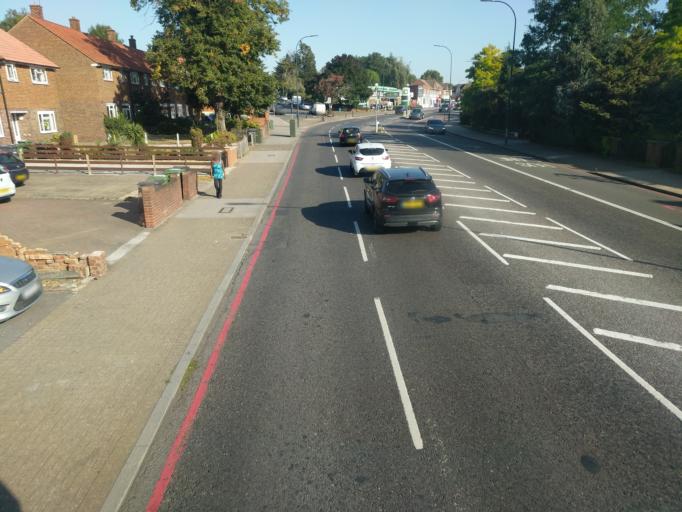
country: GB
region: England
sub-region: Greater London
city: Catford
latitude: 51.4267
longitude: -0.0086
